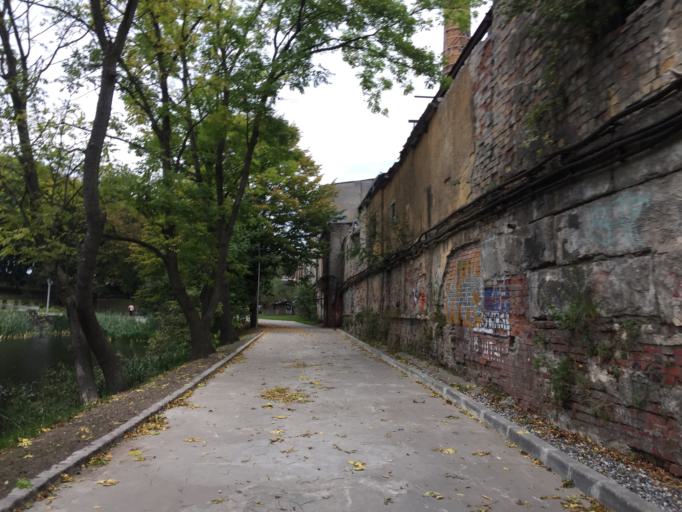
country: RU
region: Kaliningrad
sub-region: Gorod Kaliningrad
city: Kaliningrad
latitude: 54.7195
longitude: 20.5211
